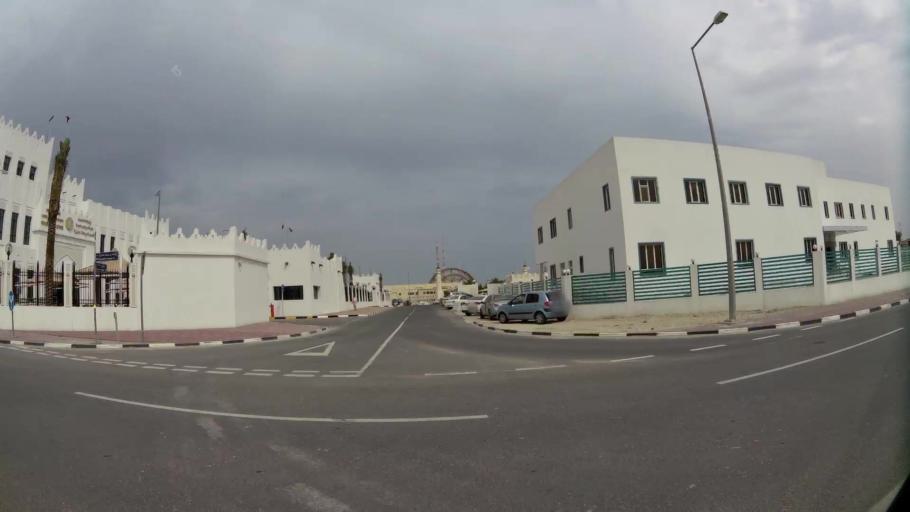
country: QA
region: Baladiyat ad Dawhah
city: Doha
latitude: 25.3361
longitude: 51.5043
